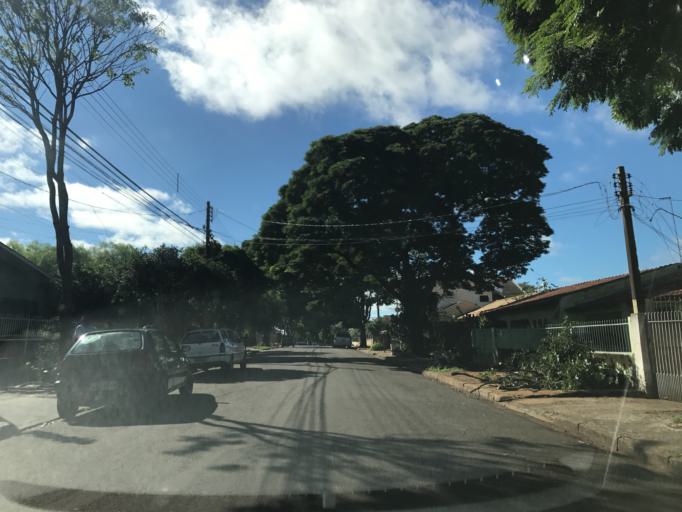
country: BR
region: Parana
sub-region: Maringa
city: Maringa
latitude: -23.4505
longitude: -51.9581
